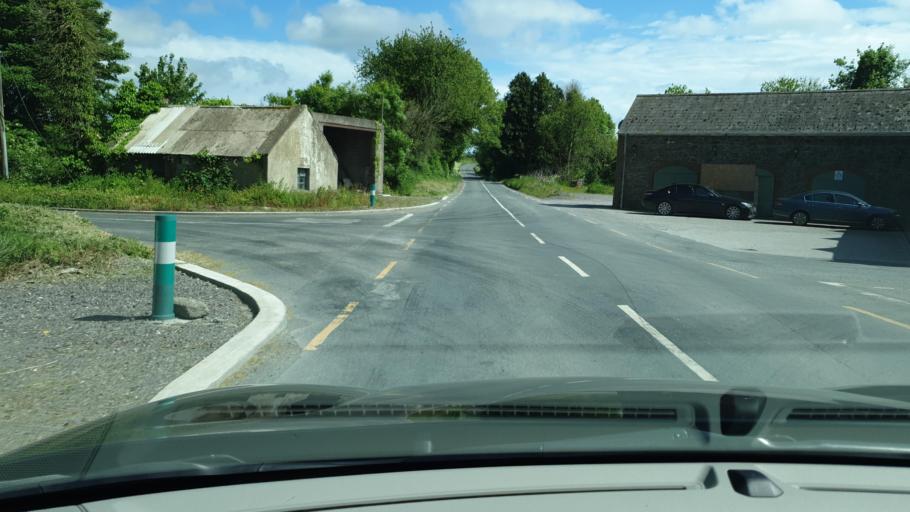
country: IE
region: Leinster
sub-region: An Mhi
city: Slane
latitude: 53.7460
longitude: -6.5964
